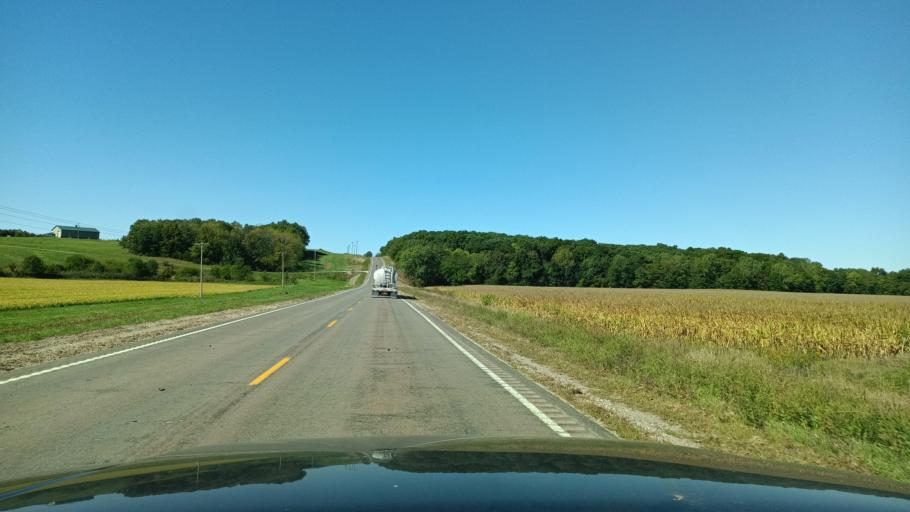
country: US
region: Missouri
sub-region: Scotland County
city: Memphis
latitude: 40.4540
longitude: -91.9983
